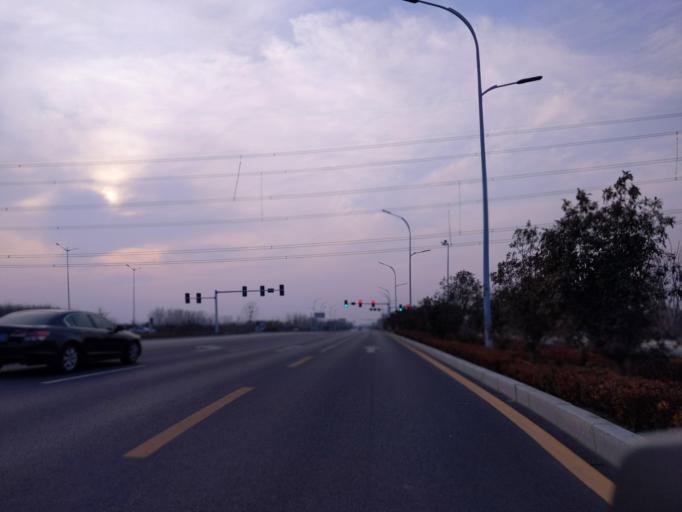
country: CN
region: Henan Sheng
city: Puyang
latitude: 35.8190
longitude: 114.9974
